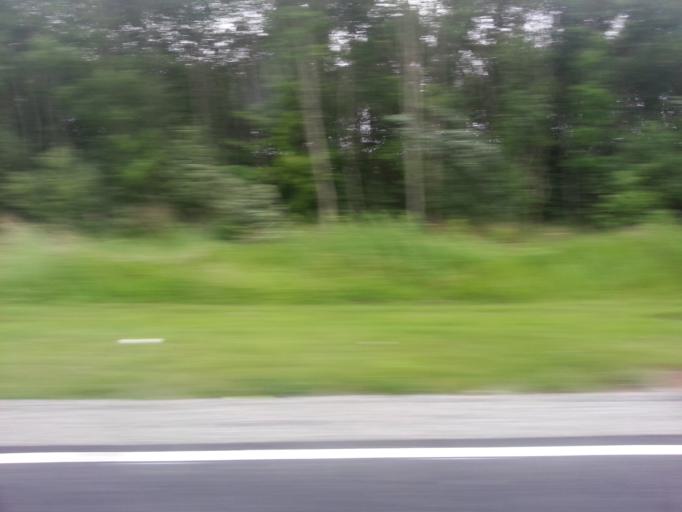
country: IE
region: Leinster
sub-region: Kildare
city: Kilcullen
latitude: 53.1673
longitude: -6.7574
